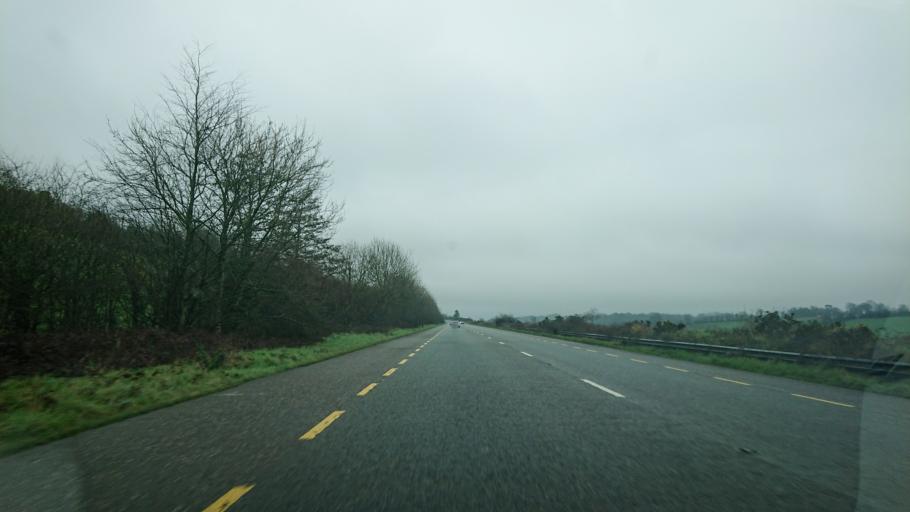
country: IE
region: Munster
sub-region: County Cork
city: Kinsale
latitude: 51.8086
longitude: -8.5516
